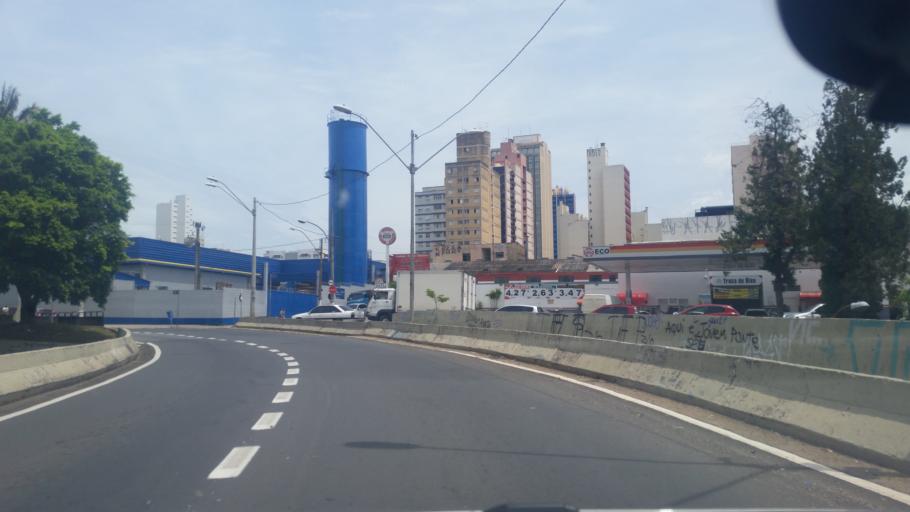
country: BR
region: Sao Paulo
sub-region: Campinas
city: Campinas
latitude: -22.9031
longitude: -47.0652
